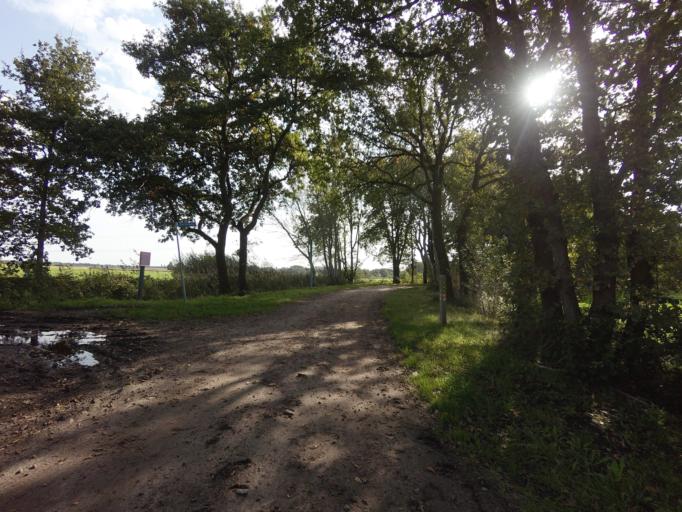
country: NL
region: North Brabant
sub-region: Gemeente Breda
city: Hoge Vucht
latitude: 51.6211
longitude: 4.7761
